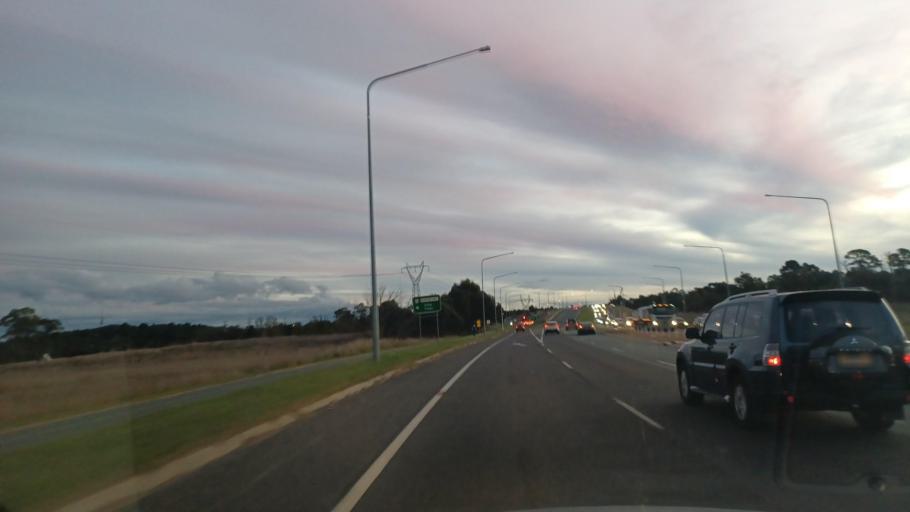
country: AU
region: Australian Capital Territory
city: Kaleen
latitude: -35.2236
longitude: 149.1271
